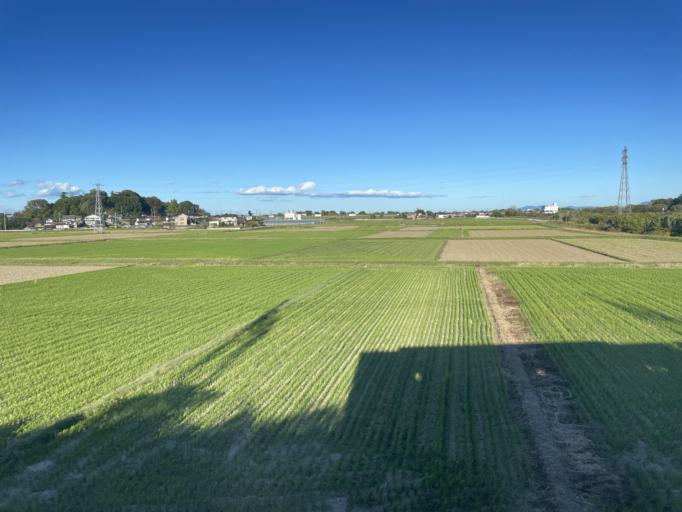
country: JP
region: Tochigi
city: Fujioka
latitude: 36.2137
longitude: 139.6507
